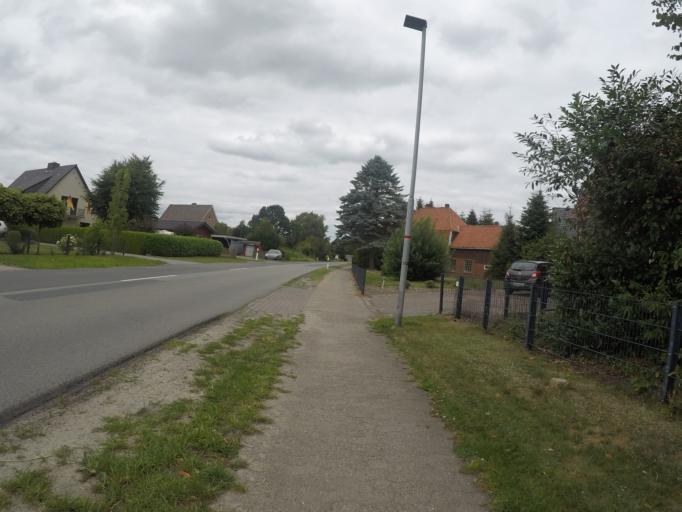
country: DE
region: Lower Saxony
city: Himmelpforten
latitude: 53.6253
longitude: 9.3083
